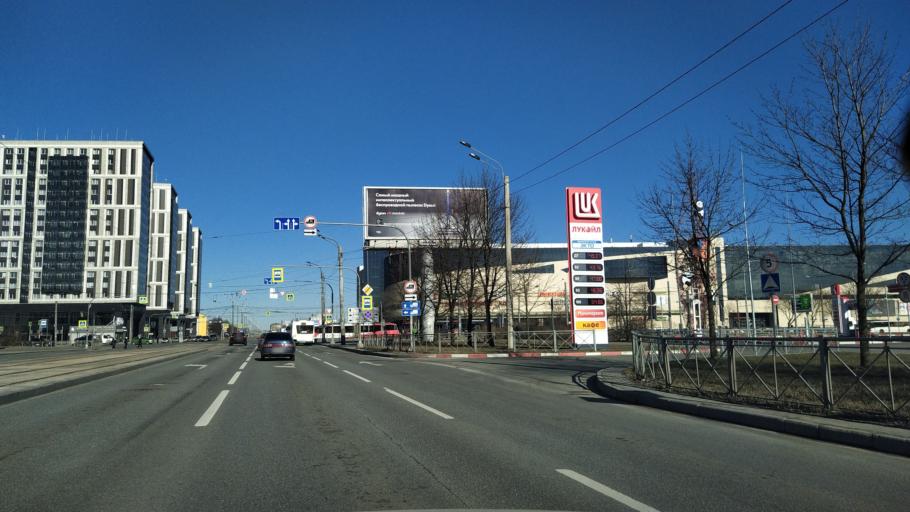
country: RU
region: St.-Petersburg
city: Kupchino
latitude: 59.8830
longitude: 30.3652
